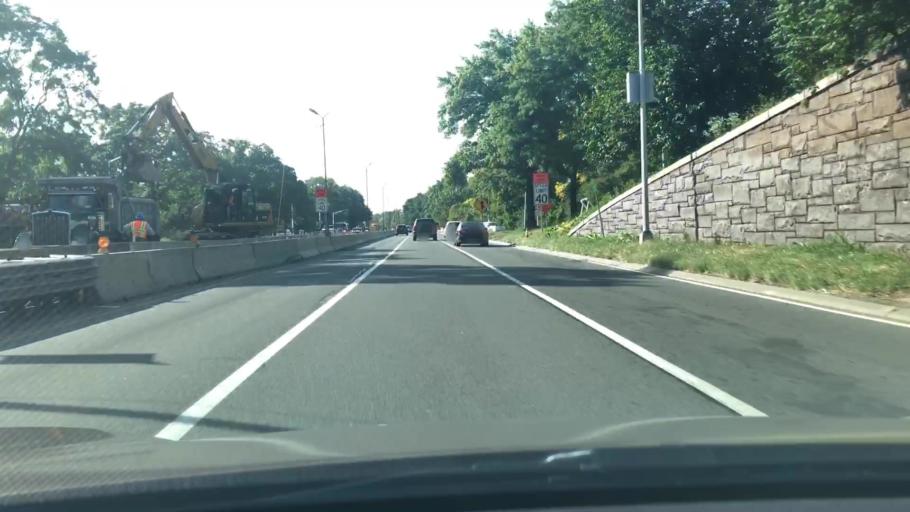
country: US
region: New York
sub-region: Bronx
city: The Bronx
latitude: 40.8781
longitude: -73.8702
